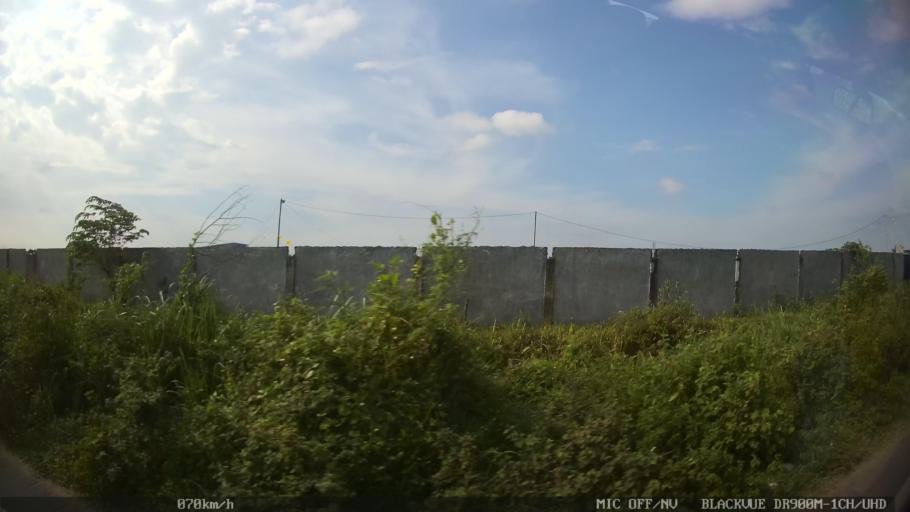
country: ID
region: North Sumatra
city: Medan
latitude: 3.5731
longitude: 98.7691
